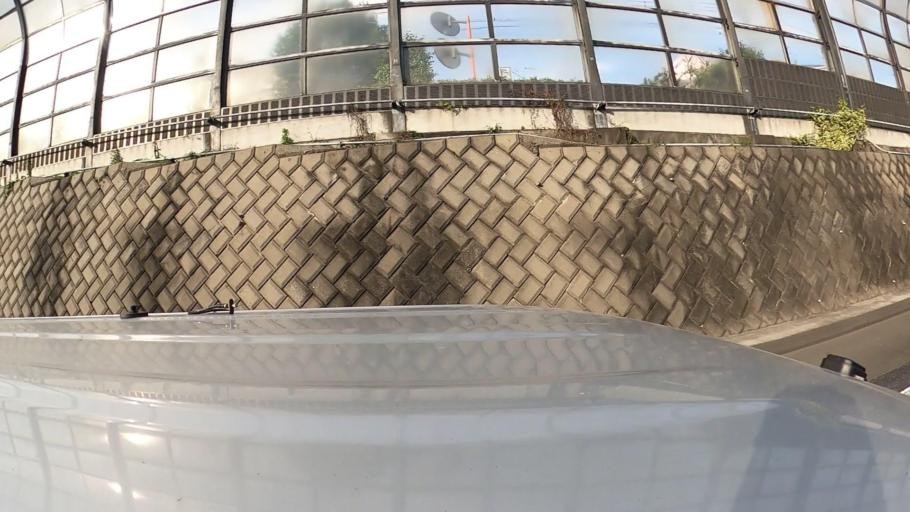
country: JP
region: Saitama
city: Asaka
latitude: 35.7679
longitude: 139.5734
